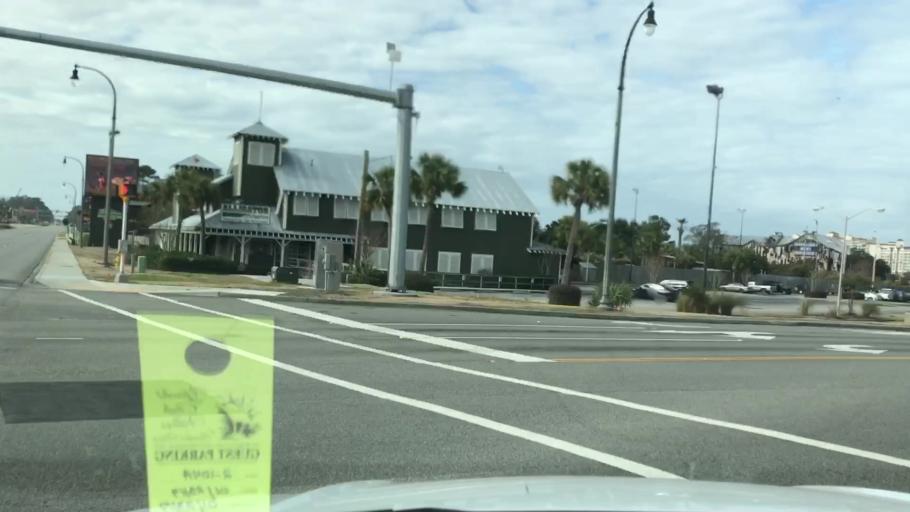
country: US
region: South Carolina
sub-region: Horry County
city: North Myrtle Beach
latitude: 33.7996
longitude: -78.7366
